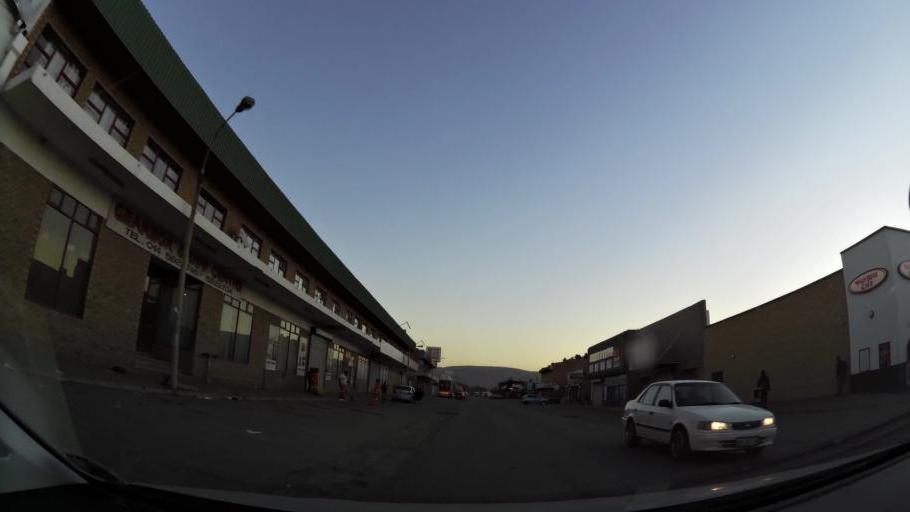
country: ZA
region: North-West
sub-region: Bojanala Platinum District Municipality
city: Rustenburg
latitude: -25.6642
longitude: 27.2411
